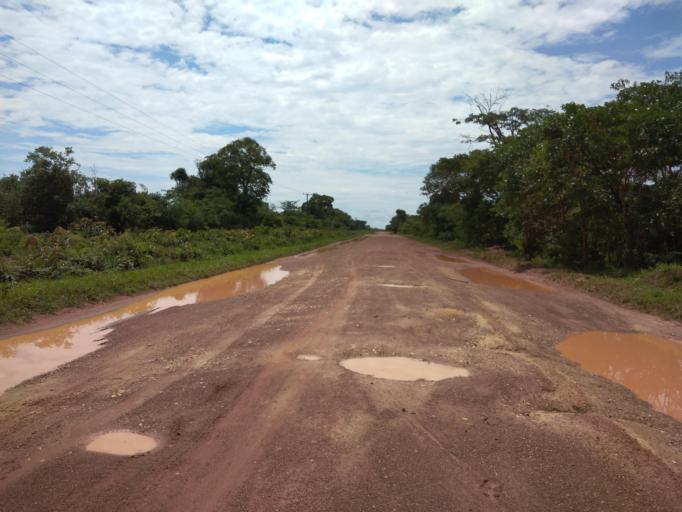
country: ZM
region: Copperbelt
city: Luanshya
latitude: -13.4816
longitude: 28.7360
